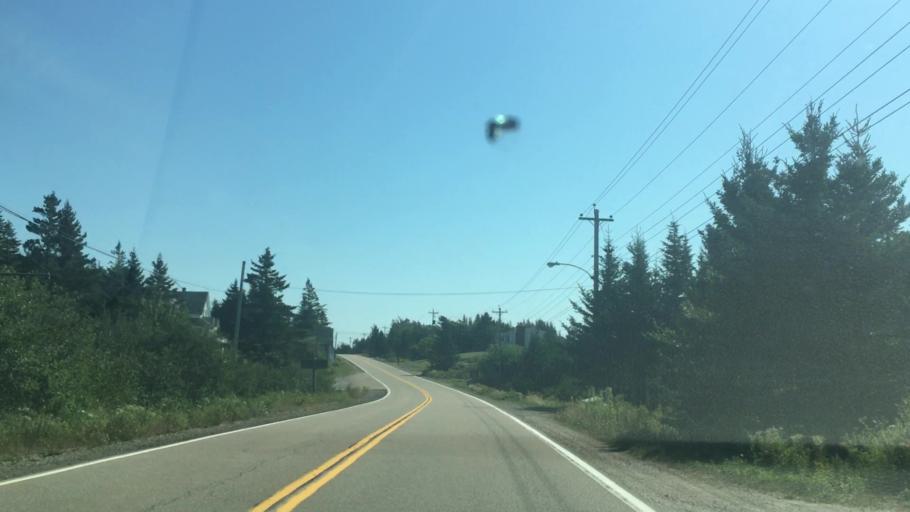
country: CA
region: Nova Scotia
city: Antigonish
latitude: 45.0252
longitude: -62.0258
